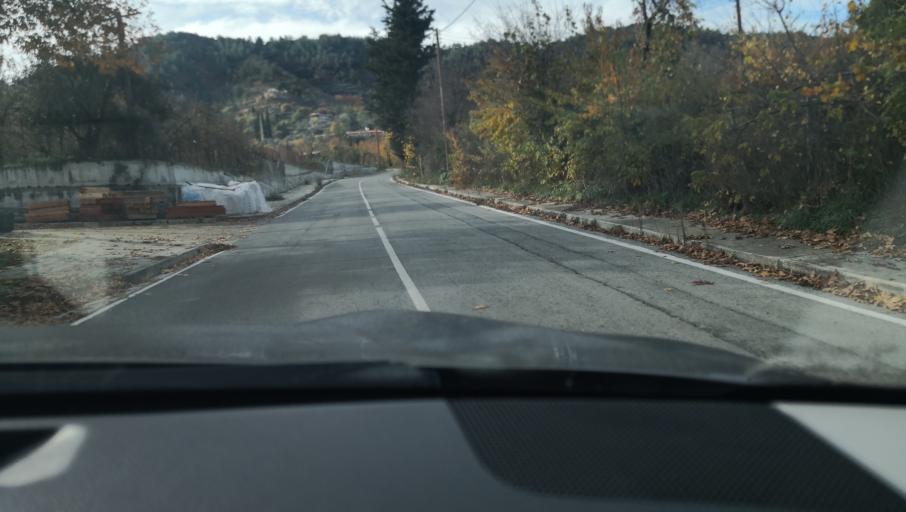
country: CY
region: Lefkosia
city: Lefka
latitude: 35.0274
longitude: 32.7275
